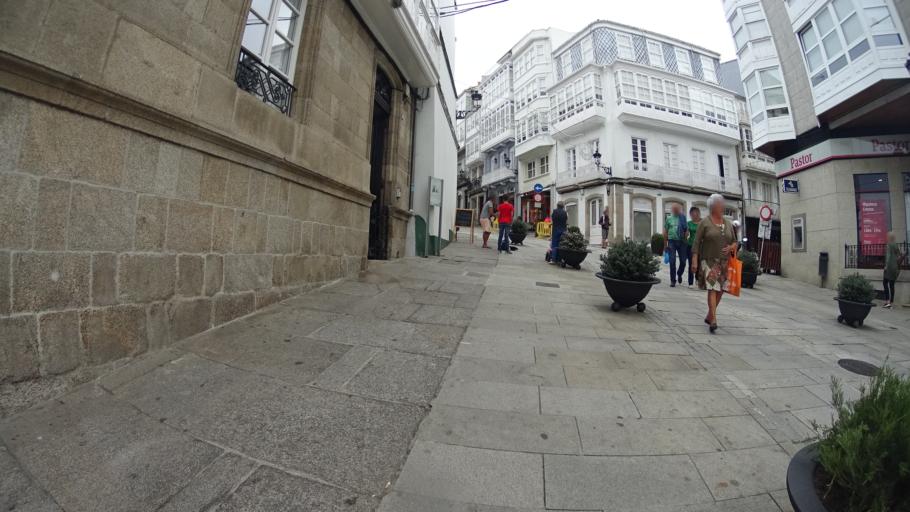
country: ES
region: Galicia
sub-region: Provincia da Coruna
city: Betanzos
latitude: 43.2802
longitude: -8.2102
